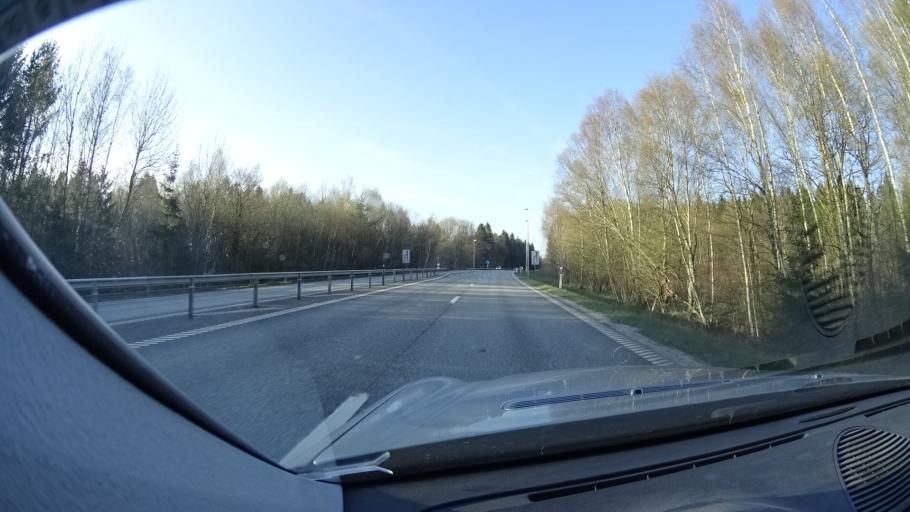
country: SE
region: Skane
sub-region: Hoors Kommun
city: Satofta
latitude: 55.9091
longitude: 13.5225
